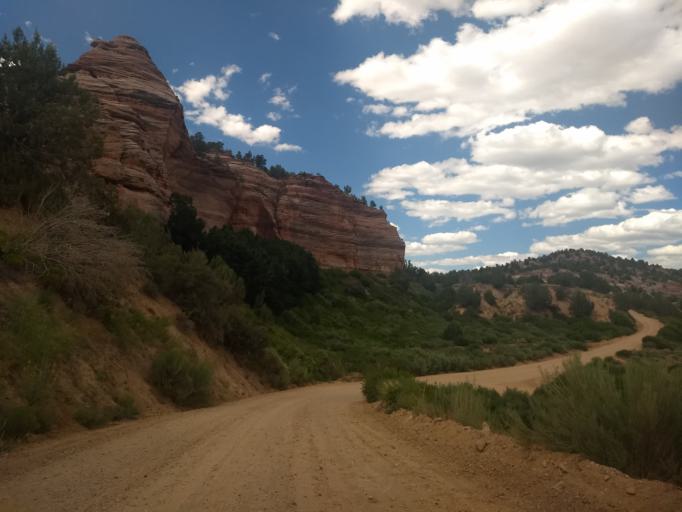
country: US
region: Utah
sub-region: Kane County
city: Kanab
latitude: 37.1448
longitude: -112.5411
